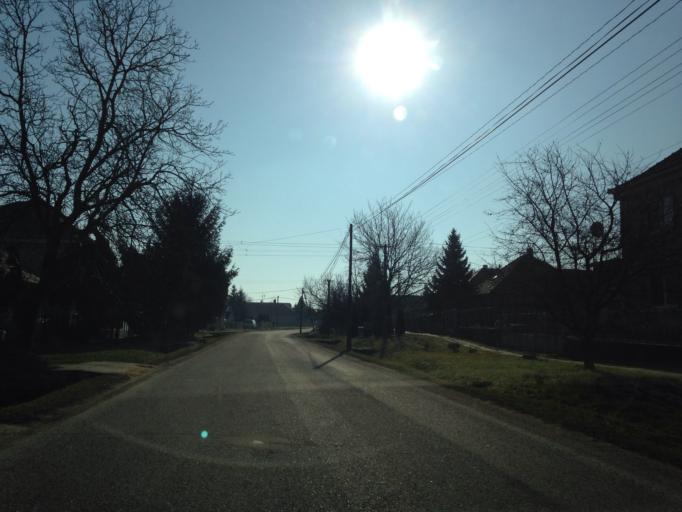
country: SK
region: Nitriansky
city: Svodin
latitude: 47.9268
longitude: 18.4018
